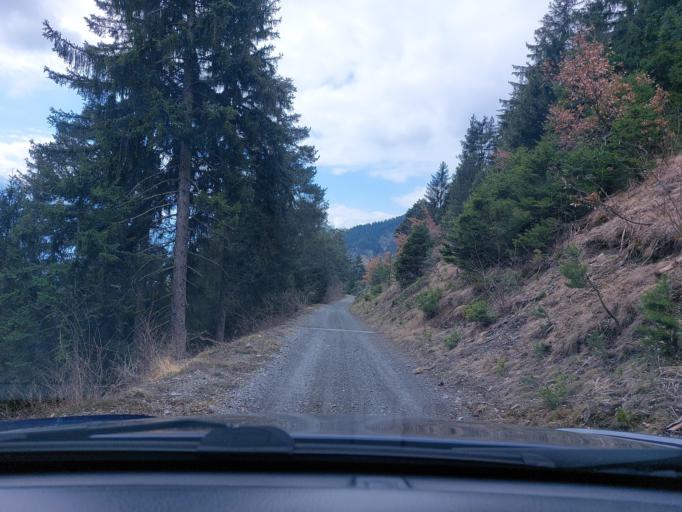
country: CH
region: Valais
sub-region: Sion District
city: Saviese
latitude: 46.2735
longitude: 7.3194
